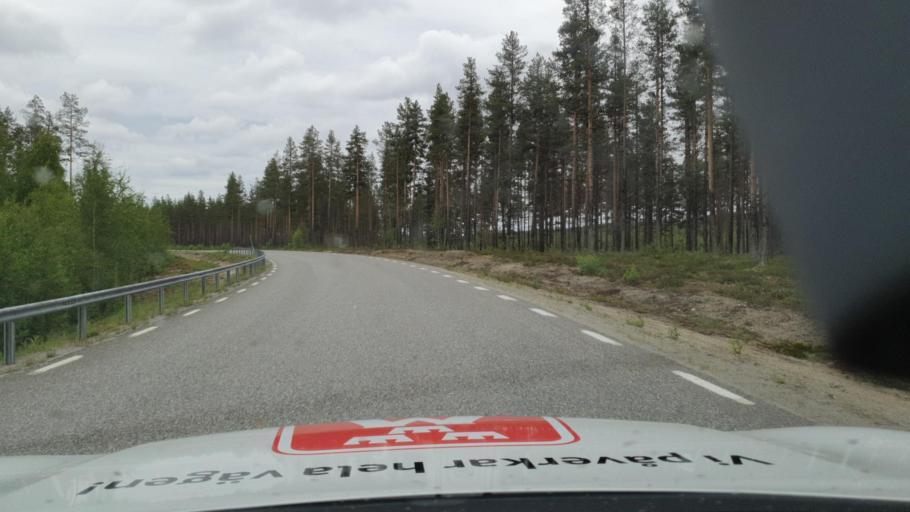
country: SE
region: Vaesterbotten
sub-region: Lycksele Kommun
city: Lycksele
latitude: 64.2130
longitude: 18.2672
